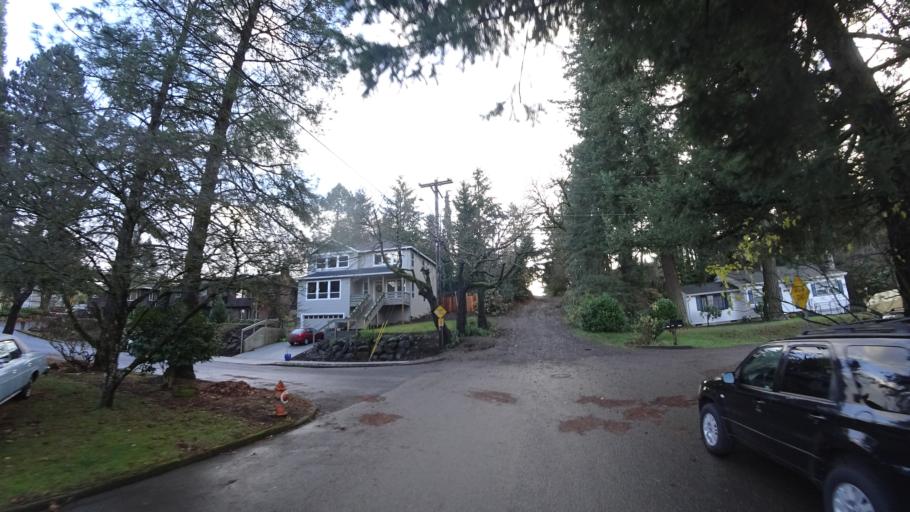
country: US
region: Oregon
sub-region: Multnomah County
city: Lents
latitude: 45.5162
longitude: -122.5494
